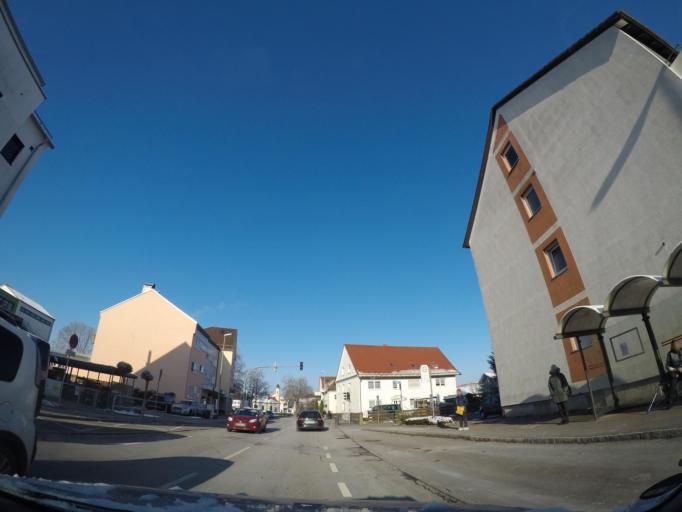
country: DE
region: Bavaria
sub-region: Swabia
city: Senden
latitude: 48.3232
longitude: 10.0363
